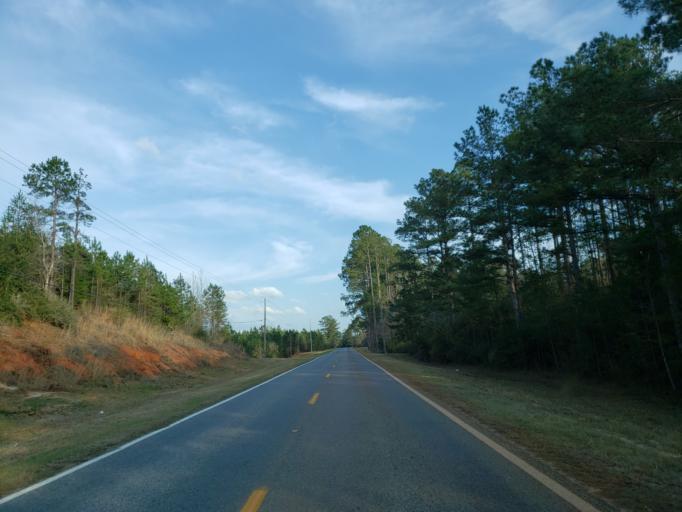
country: US
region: Mississippi
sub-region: Clarke County
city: Stonewall
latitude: 32.1757
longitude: -88.7925
